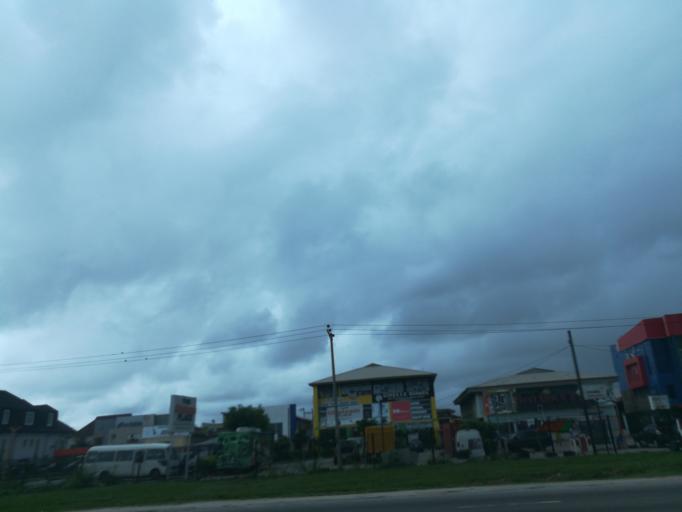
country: NG
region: Lagos
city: Ikoyi
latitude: 6.4322
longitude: 3.4780
